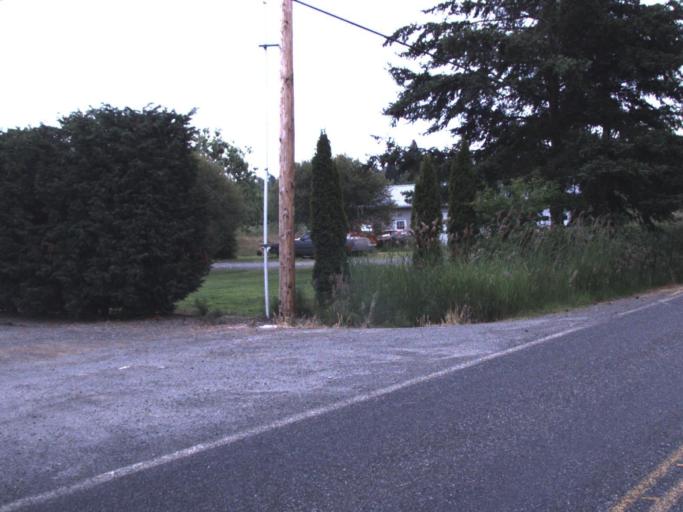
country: US
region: Washington
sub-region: Whatcom County
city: Birch Bay
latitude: 48.9248
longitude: -122.7264
